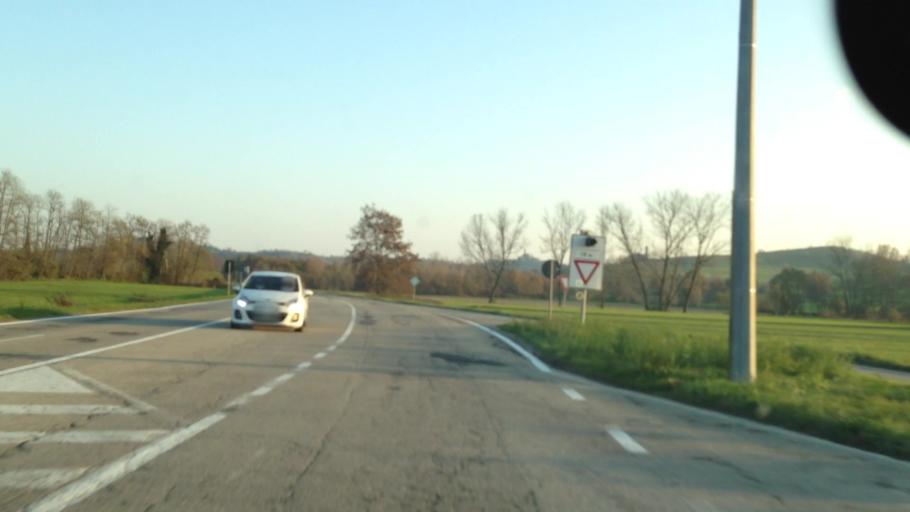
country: IT
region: Piedmont
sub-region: Provincia di Asti
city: Cunico
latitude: 45.0343
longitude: 8.1151
